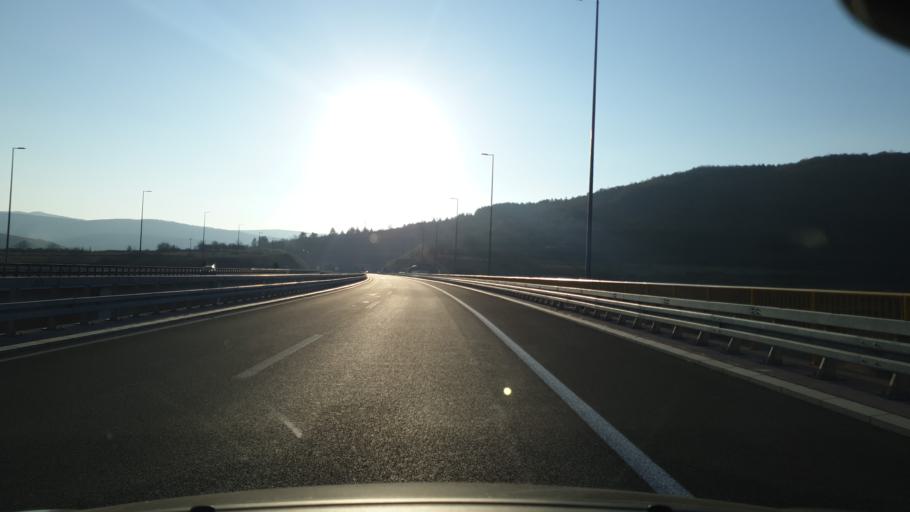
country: RS
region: Central Serbia
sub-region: Pirotski Okrug
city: Dimitrovgrad
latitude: 43.0251
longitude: 22.7792
